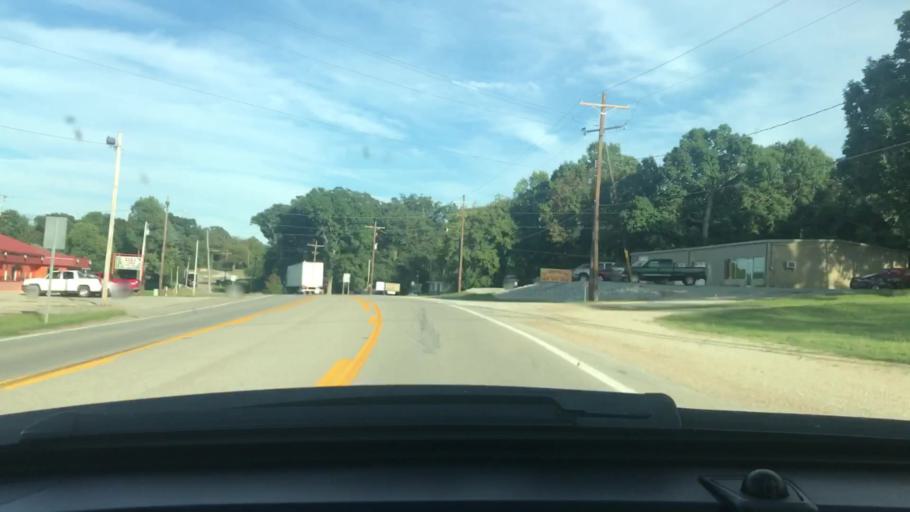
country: US
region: Arkansas
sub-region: Randolph County
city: Pocahontas
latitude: 36.2042
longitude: -91.1912
